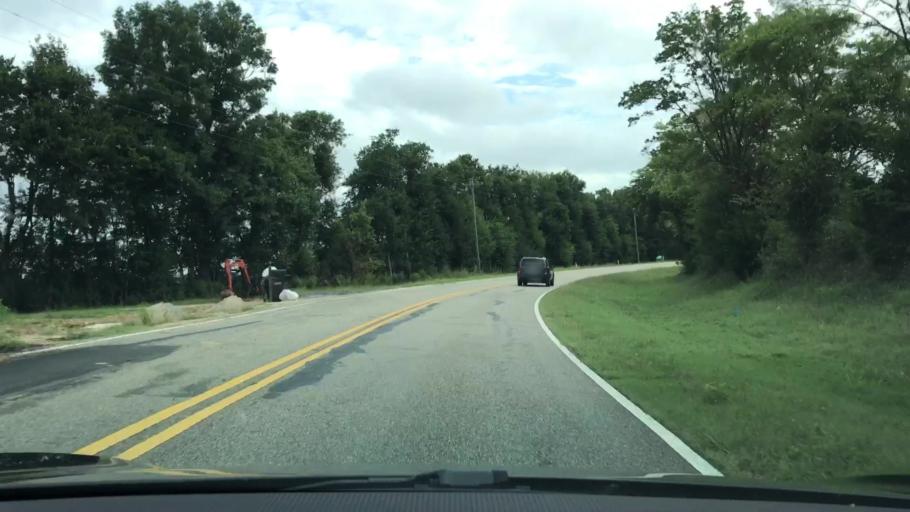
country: US
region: Alabama
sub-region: Montgomery County
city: Pike Road
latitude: 32.2999
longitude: -86.0725
